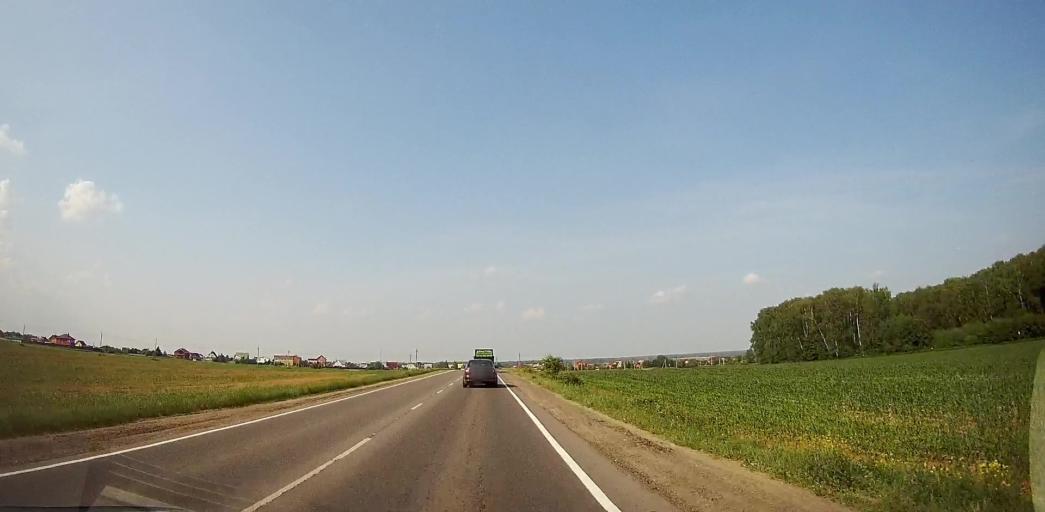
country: RU
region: Moskovskaya
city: Zhitnevo
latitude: 55.3329
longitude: 37.9060
